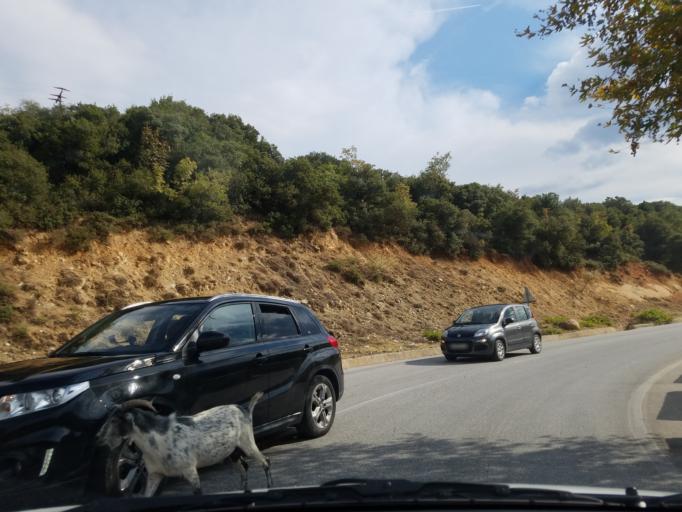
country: GR
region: Thessaly
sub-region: Trikala
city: Kalampaka
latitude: 39.7188
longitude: 21.6431
